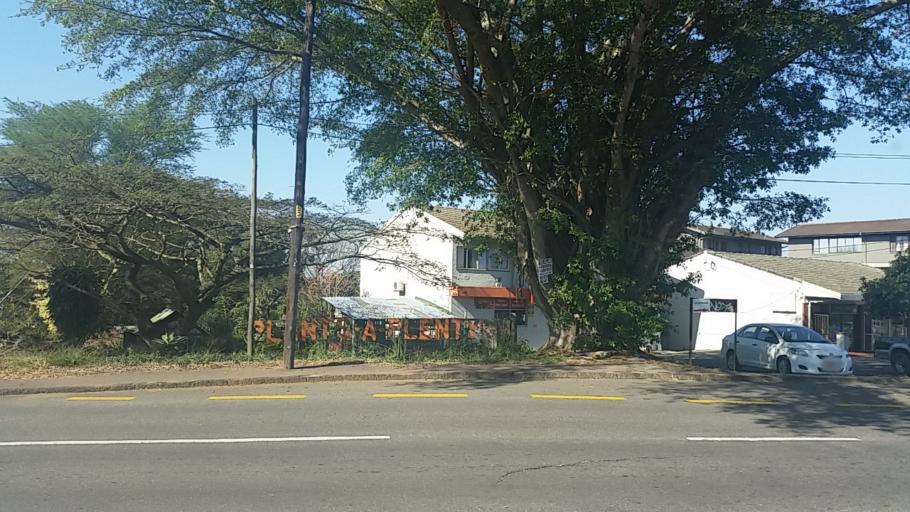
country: ZA
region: KwaZulu-Natal
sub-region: eThekwini Metropolitan Municipality
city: Berea
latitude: -29.8416
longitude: 30.9059
